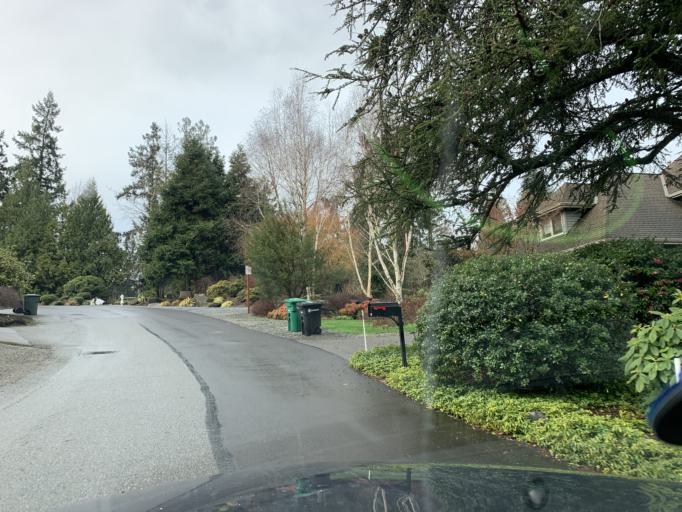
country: US
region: Washington
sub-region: King County
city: Mercer Island
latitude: 47.5928
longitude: -122.2319
